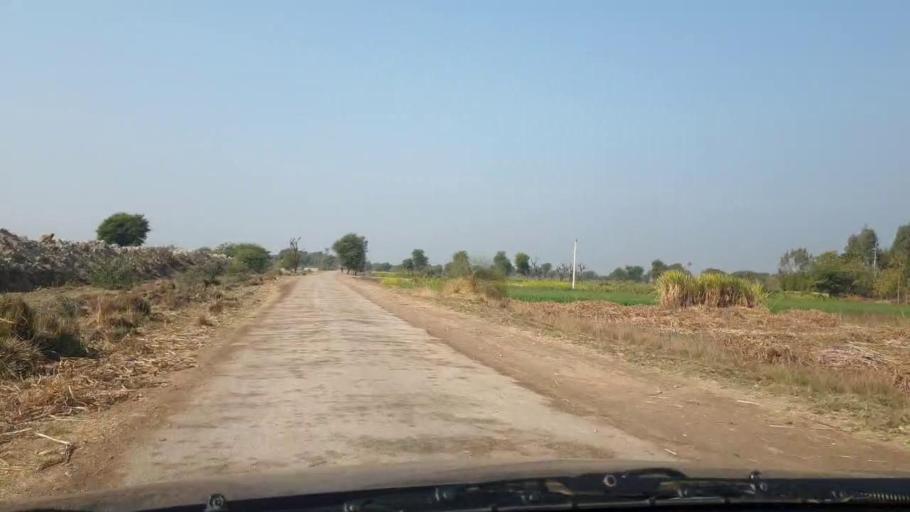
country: PK
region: Sindh
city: Jhol
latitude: 25.9612
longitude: 68.9482
